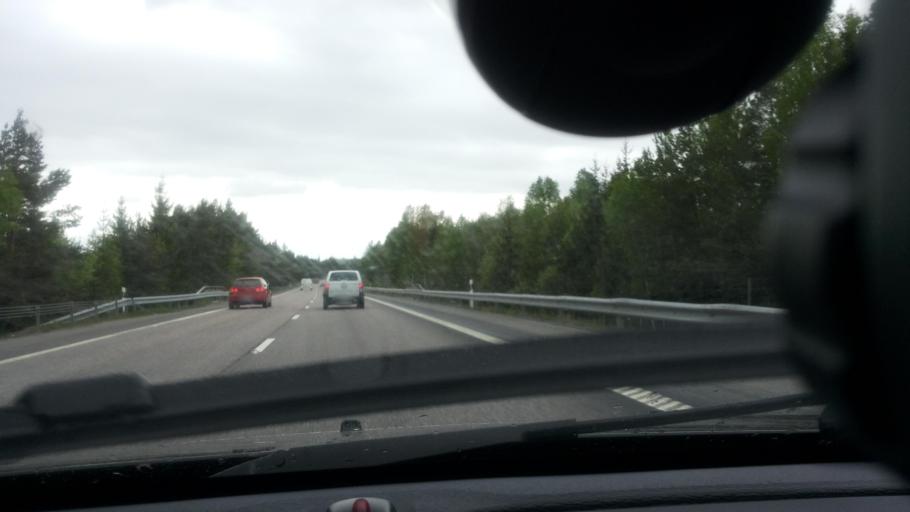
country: SE
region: Uppsala
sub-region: Knivsta Kommun
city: Knivsta
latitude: 59.7003
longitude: 17.8608
